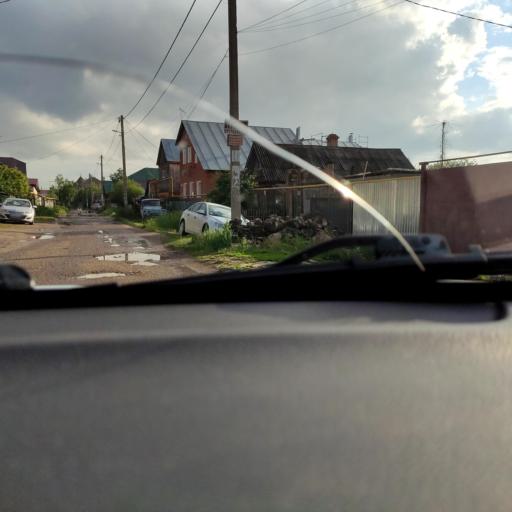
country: RU
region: Tatarstan
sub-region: Gorod Kazan'
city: Kazan
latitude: 55.8538
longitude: 49.1895
